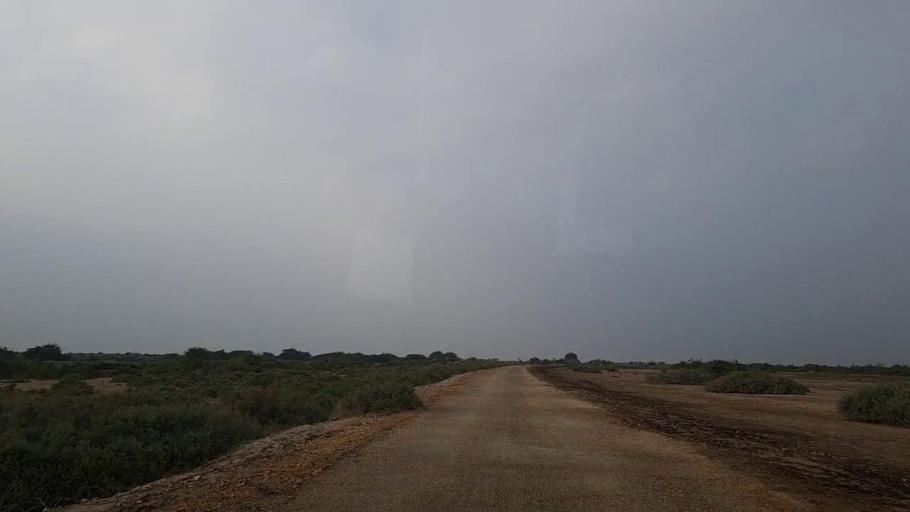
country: PK
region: Sindh
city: Mirpur Sakro
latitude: 24.6048
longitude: 67.5168
